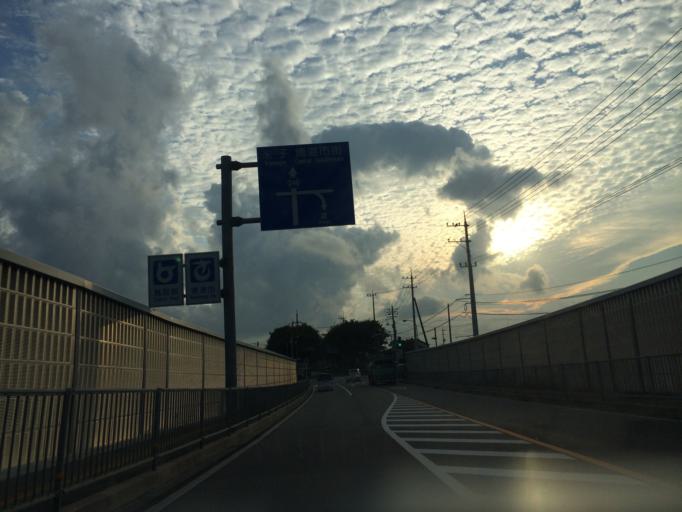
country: JP
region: Shimane
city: Sakaiminato
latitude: 35.5211
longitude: 133.2086
